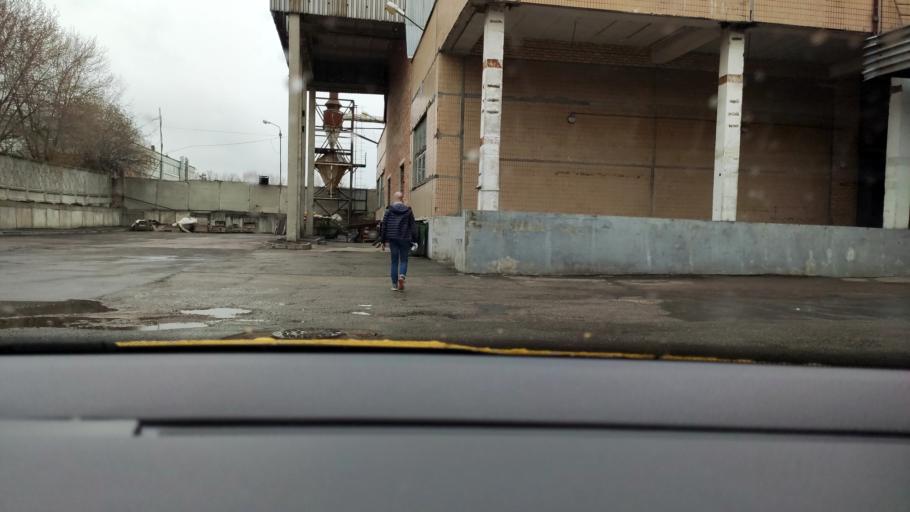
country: RU
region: Moscow
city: Tsaritsyno
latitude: 55.6380
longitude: 37.6425
